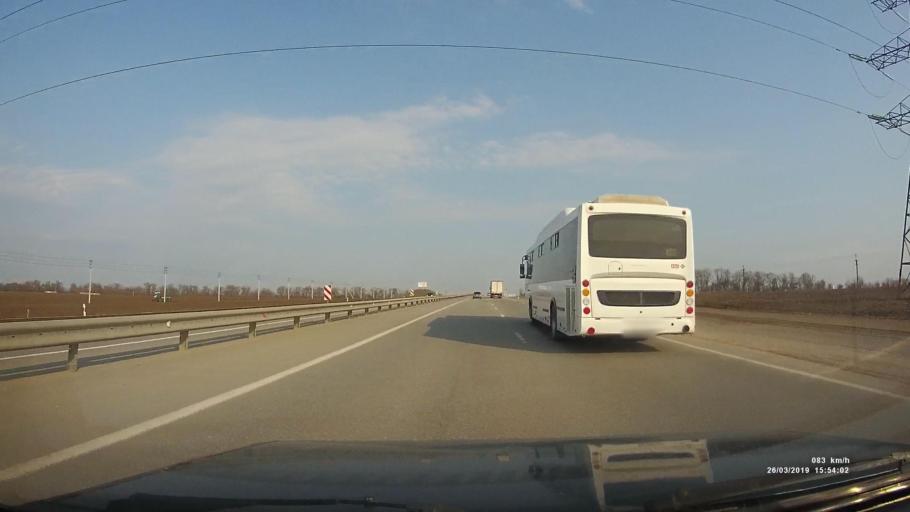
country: RU
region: Rostov
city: Krym
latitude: 47.2712
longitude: 39.5507
